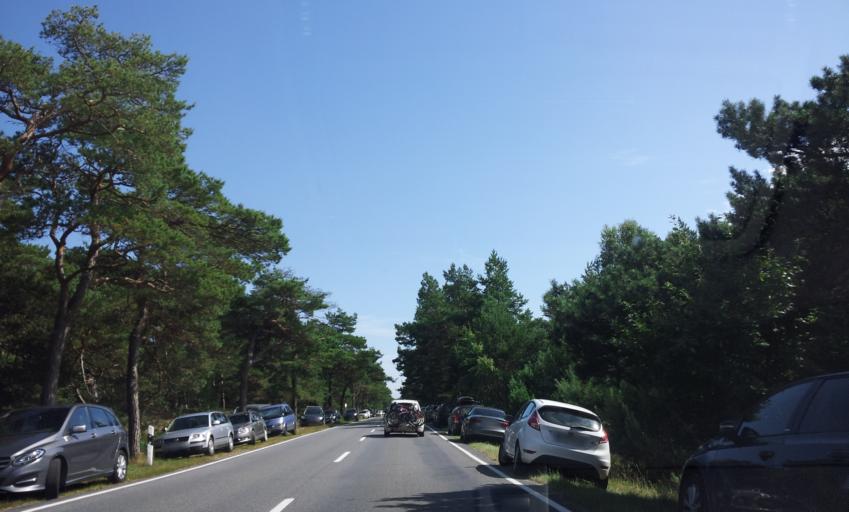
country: DE
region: Mecklenburg-Vorpommern
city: Altenkirchen
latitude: 54.5947
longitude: 13.3914
